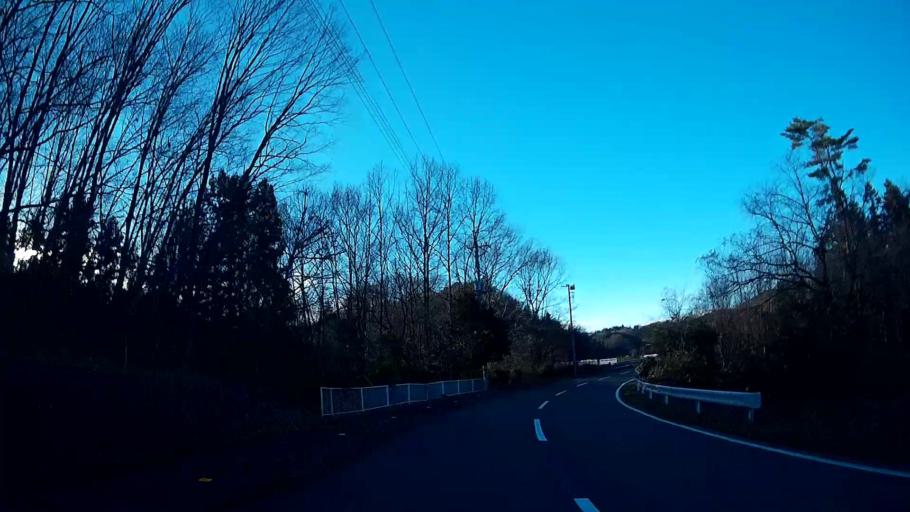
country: JP
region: Saitama
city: Chichibu
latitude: 36.0354
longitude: 139.0174
